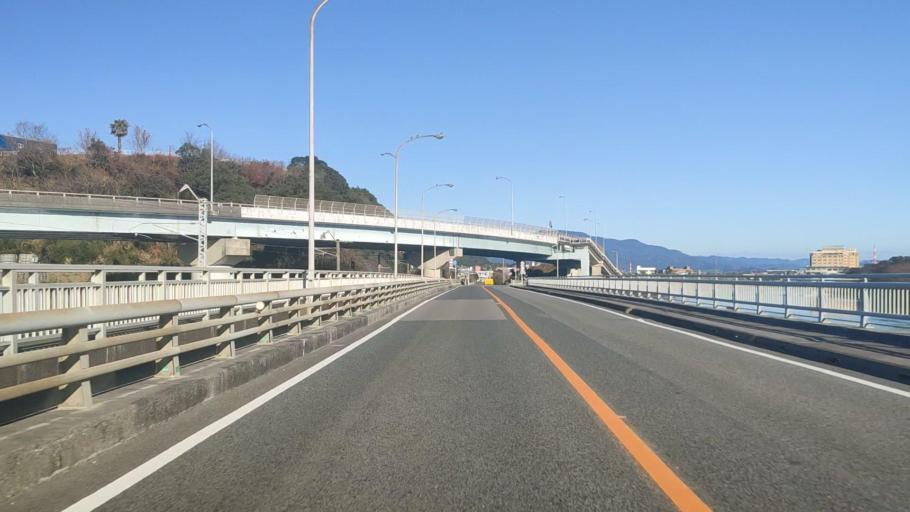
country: JP
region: Miyazaki
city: Nobeoka
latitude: 32.5361
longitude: 131.6796
